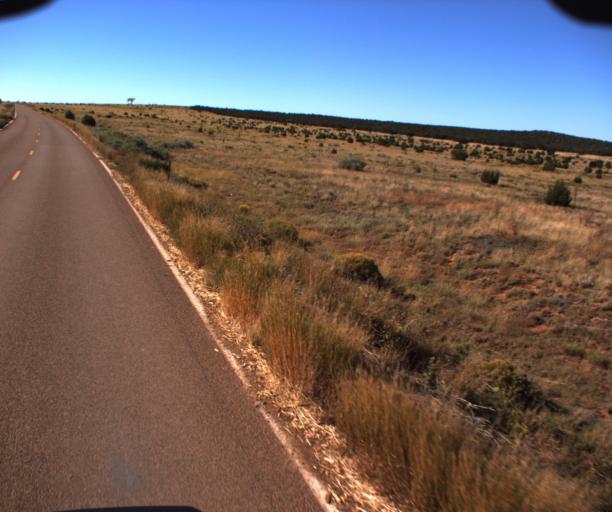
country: US
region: Arizona
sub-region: Navajo County
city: Heber-Overgaard
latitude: 34.4936
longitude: -110.3405
